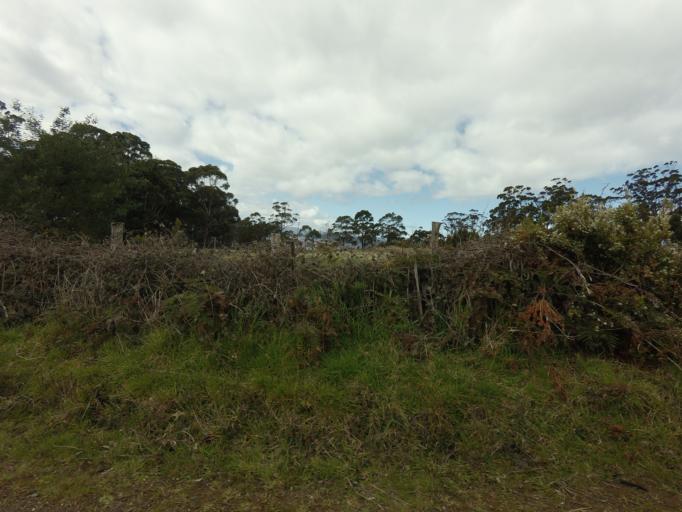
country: AU
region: Tasmania
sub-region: Huon Valley
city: Cygnet
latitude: -43.4124
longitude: 147.0183
